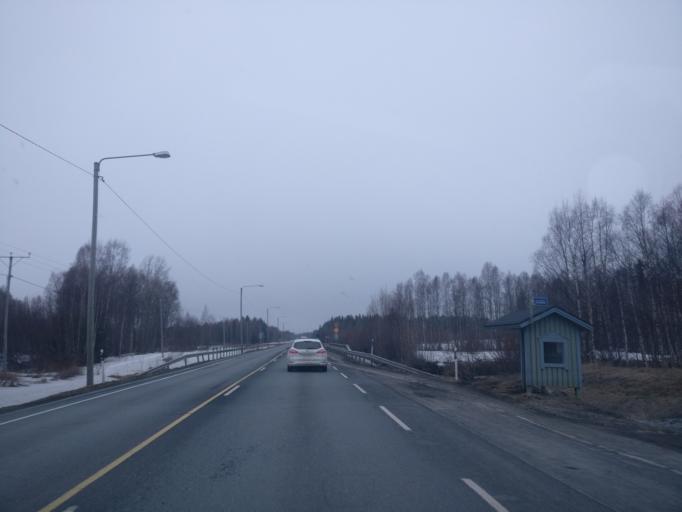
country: FI
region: Lapland
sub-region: Kemi-Tornio
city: Simo
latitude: 65.6698
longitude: 24.9264
